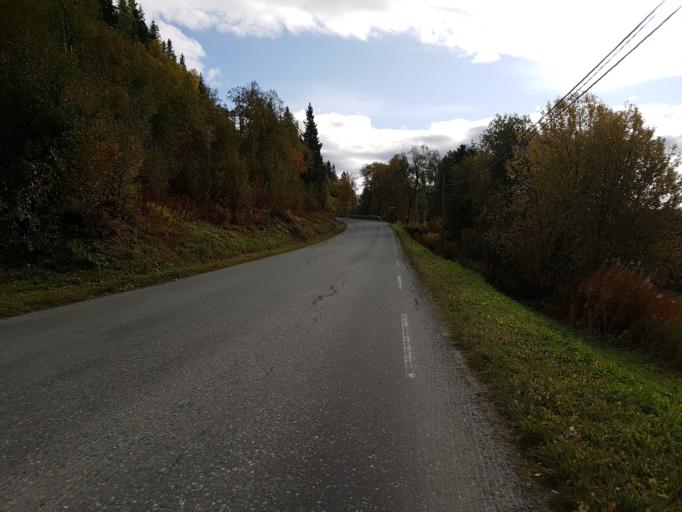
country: NO
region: Sor-Trondelag
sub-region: Klaebu
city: Klaebu
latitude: 63.3941
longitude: 10.5554
